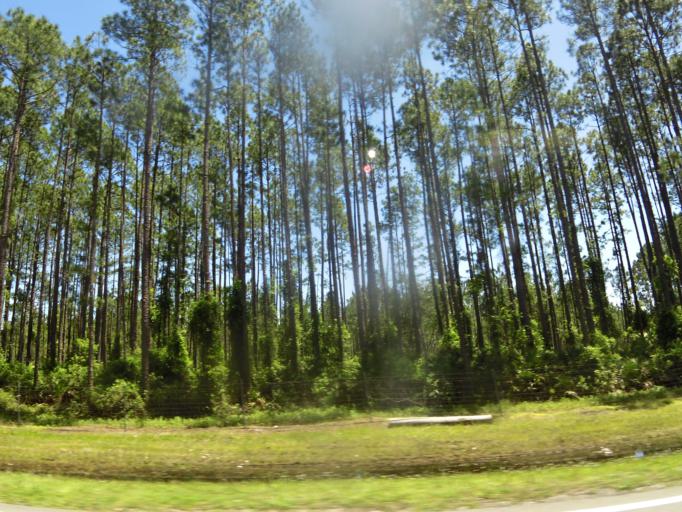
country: US
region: Florida
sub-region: Saint Johns County
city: Fruit Cove
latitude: 30.0378
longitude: -81.5842
